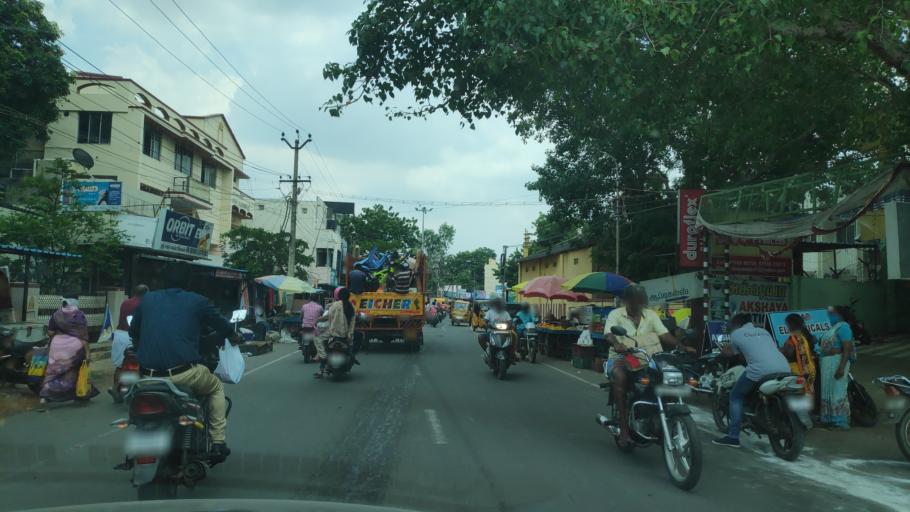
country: IN
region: Tamil Nadu
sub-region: Thiruvallur
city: Ambattur
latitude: 13.1183
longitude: 80.1525
